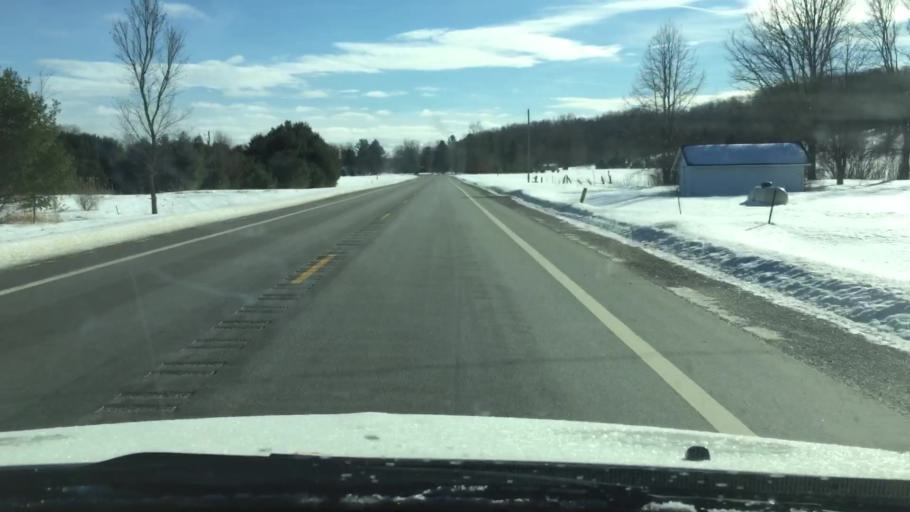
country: US
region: Michigan
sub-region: Charlevoix County
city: East Jordan
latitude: 45.0711
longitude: -85.0856
